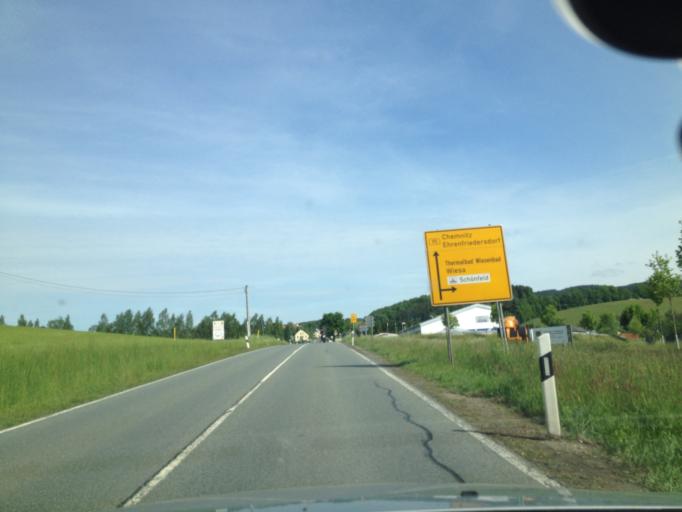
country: DE
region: Saxony
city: Wiesa
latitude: 50.6058
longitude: 12.9935
